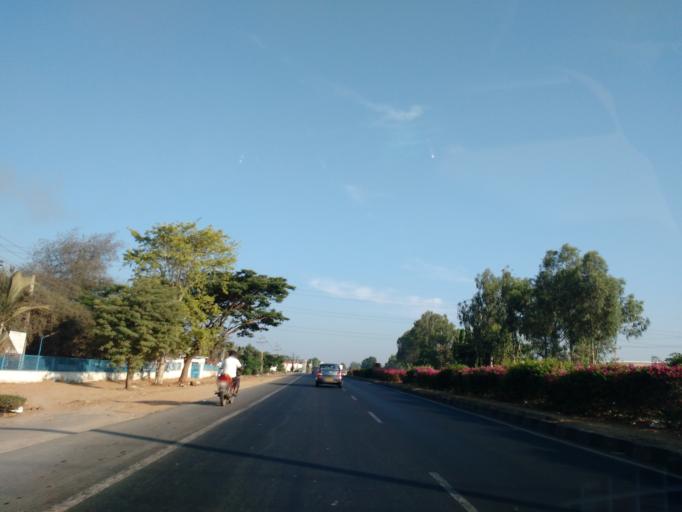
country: IN
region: Karnataka
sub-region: Bangalore Rural
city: Nelamangala
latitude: 13.1318
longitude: 77.3582
